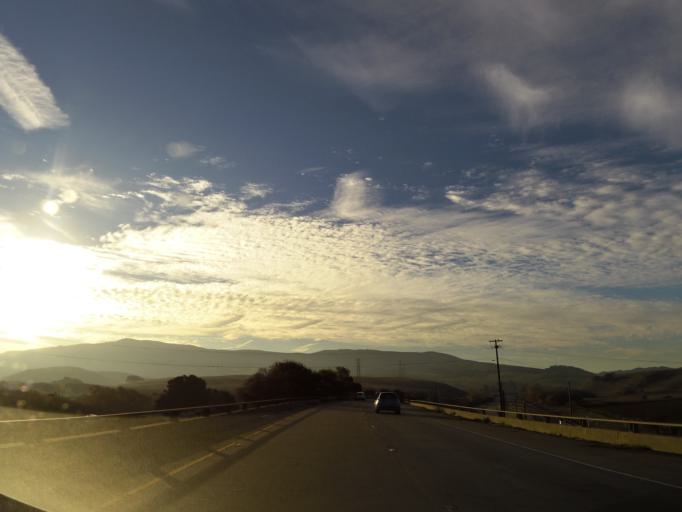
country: US
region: California
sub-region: Santa Clara County
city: Gilroy
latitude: 36.9291
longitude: -121.5481
